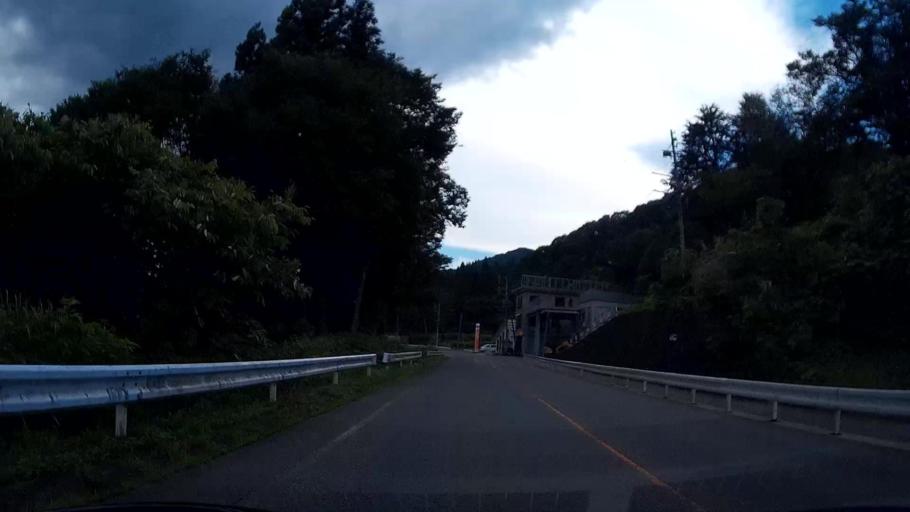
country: JP
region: Nagano
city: Iiyama
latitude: 36.9854
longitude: 138.5301
